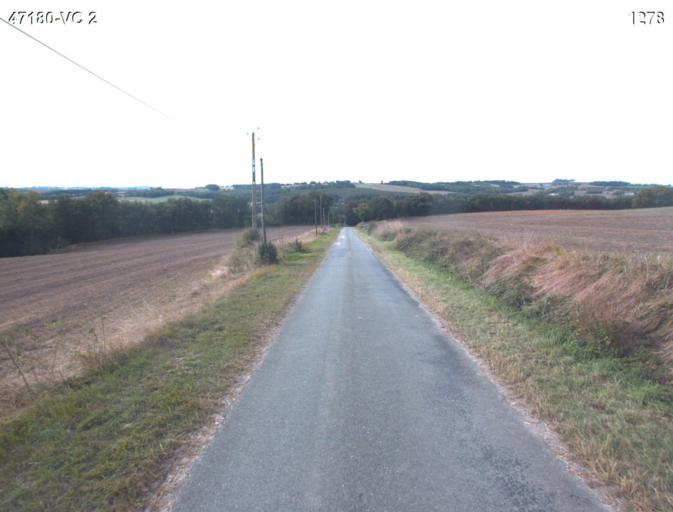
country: FR
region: Aquitaine
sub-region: Departement du Lot-et-Garonne
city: Sainte-Colombe-en-Bruilhois
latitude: 44.1670
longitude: 0.4349
